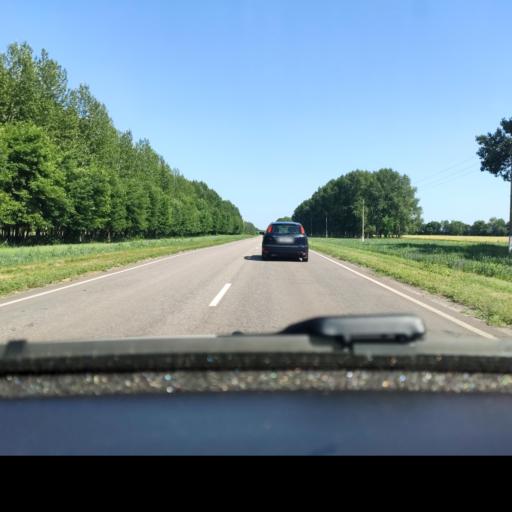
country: RU
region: Voronezj
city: Panino
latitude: 51.6644
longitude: 39.9749
